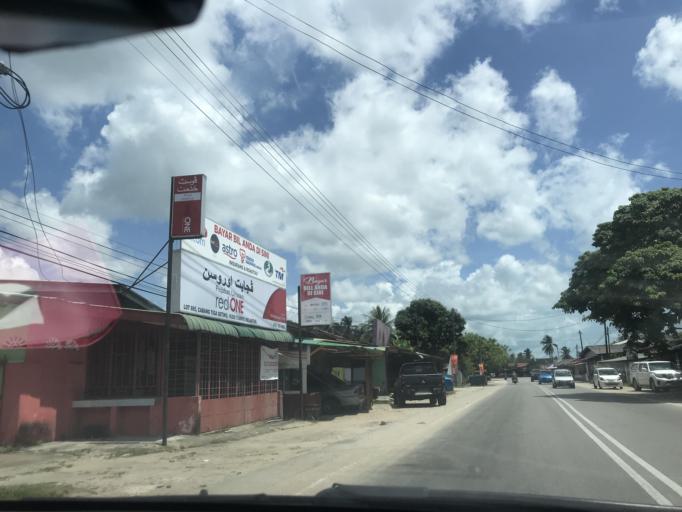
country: MY
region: Kelantan
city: Tumpat
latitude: 6.2201
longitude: 102.1121
